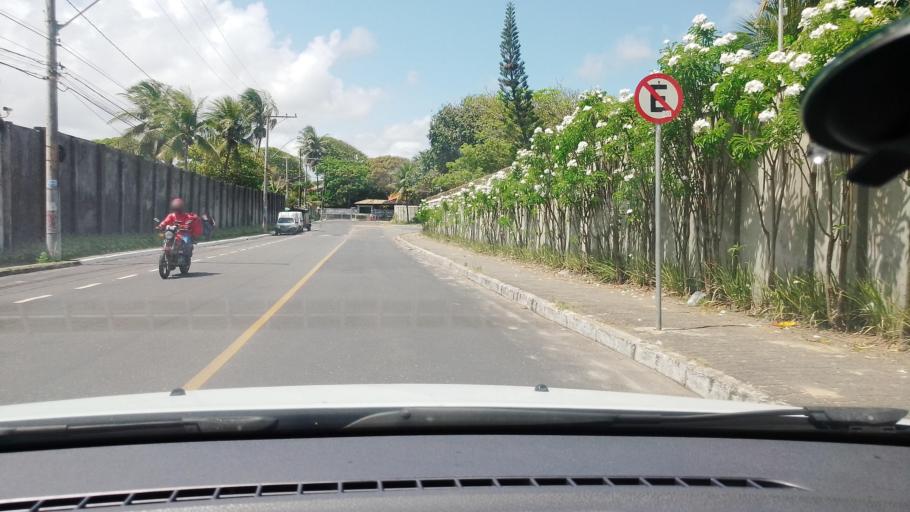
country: BR
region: Bahia
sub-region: Lauro De Freitas
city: Lauro de Freitas
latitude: -12.9551
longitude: -38.3927
